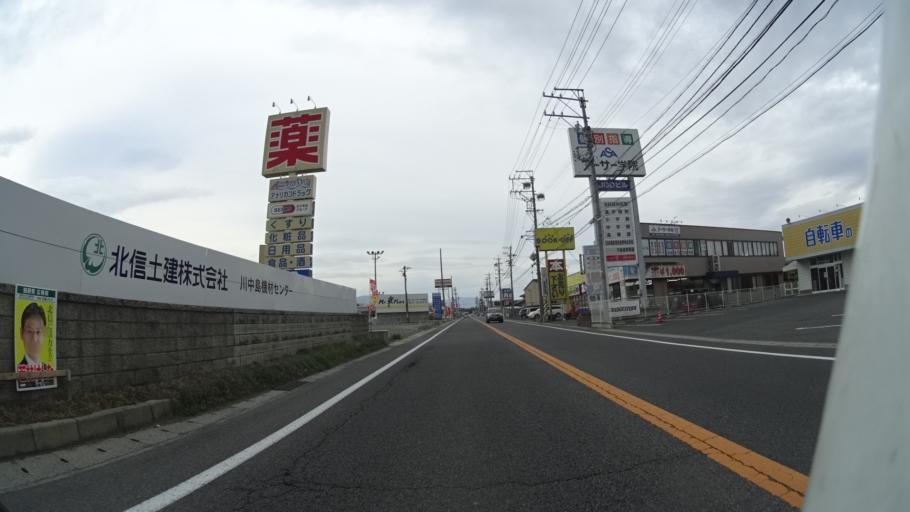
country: JP
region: Nagano
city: Nagano-shi
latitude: 36.6001
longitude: 138.1593
